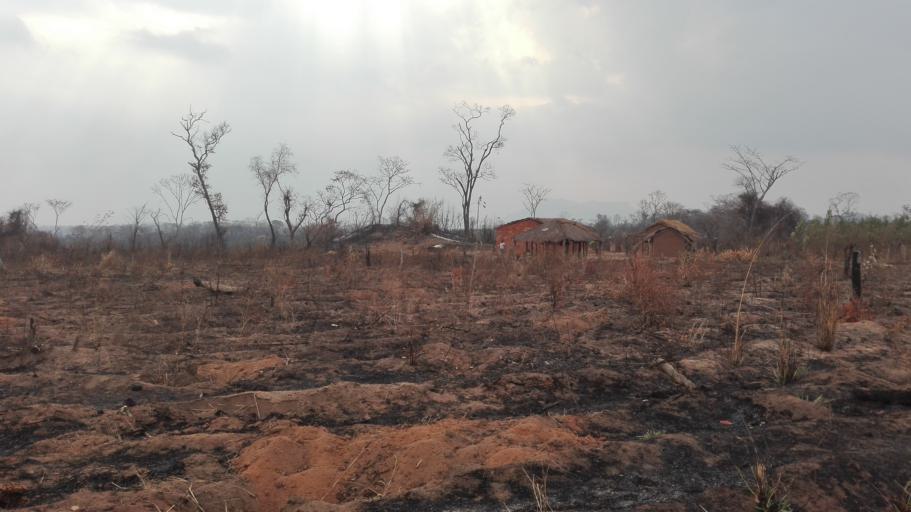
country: MZ
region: Nampula
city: Mutuali
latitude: -15.6410
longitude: 36.9225
